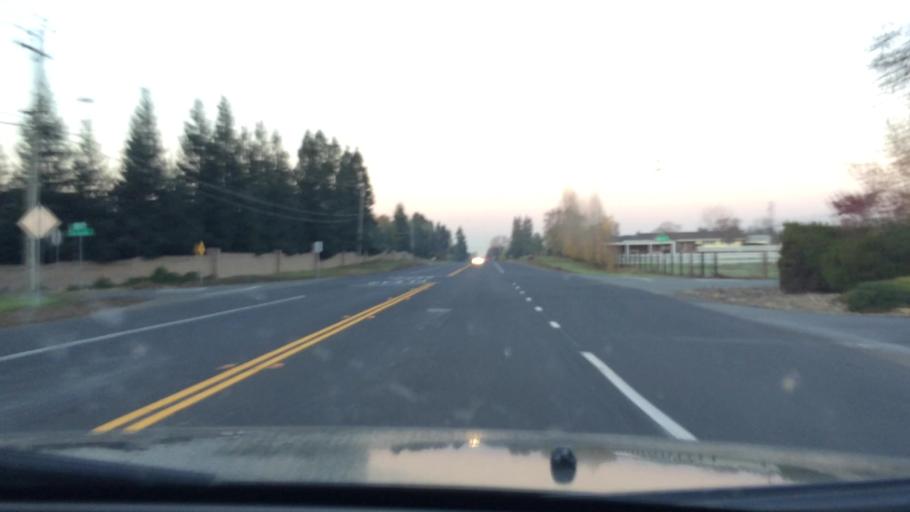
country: US
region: California
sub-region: Sacramento County
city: Vineyard
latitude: 38.4382
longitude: -121.3571
